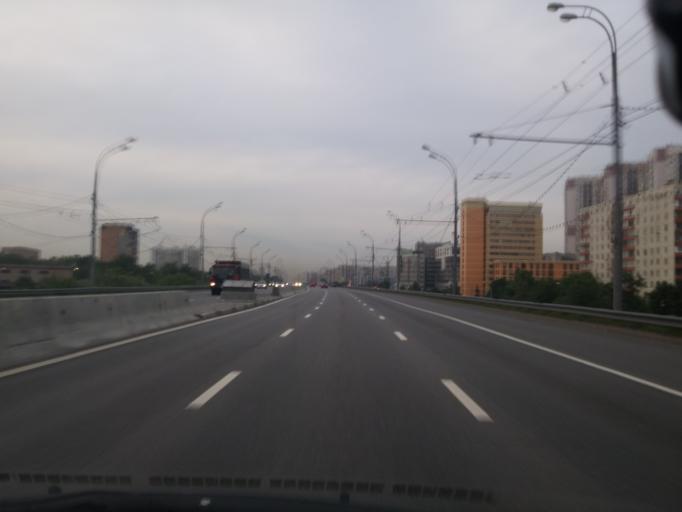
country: RU
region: Moscow
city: Slobodka
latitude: 55.8720
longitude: 37.5859
